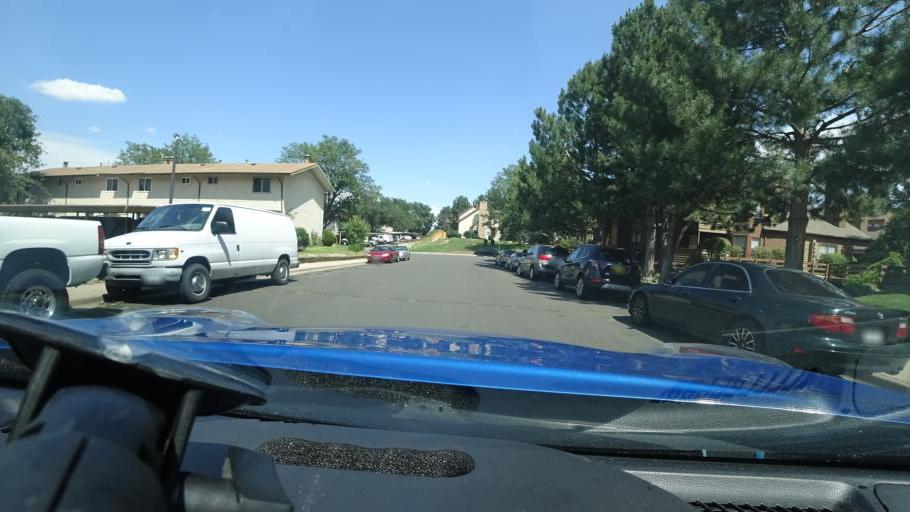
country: US
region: Colorado
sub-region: Adams County
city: Aurora
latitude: 39.6802
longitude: -104.8494
